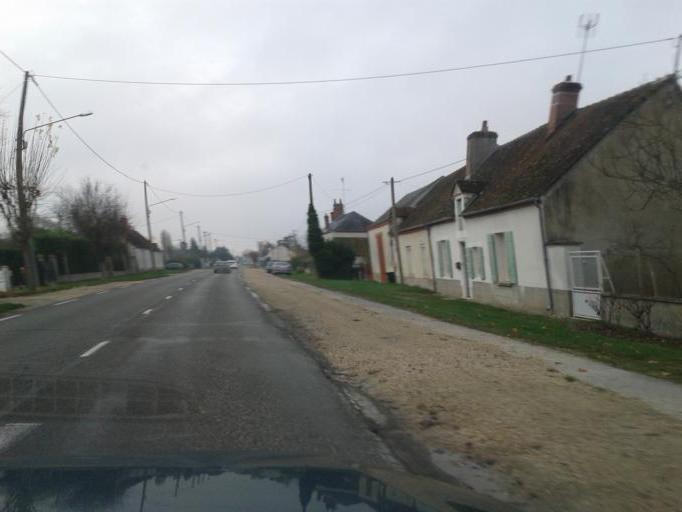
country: FR
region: Centre
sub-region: Departement du Loiret
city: Lailly-en-Val
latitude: 47.7746
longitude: 1.6974
